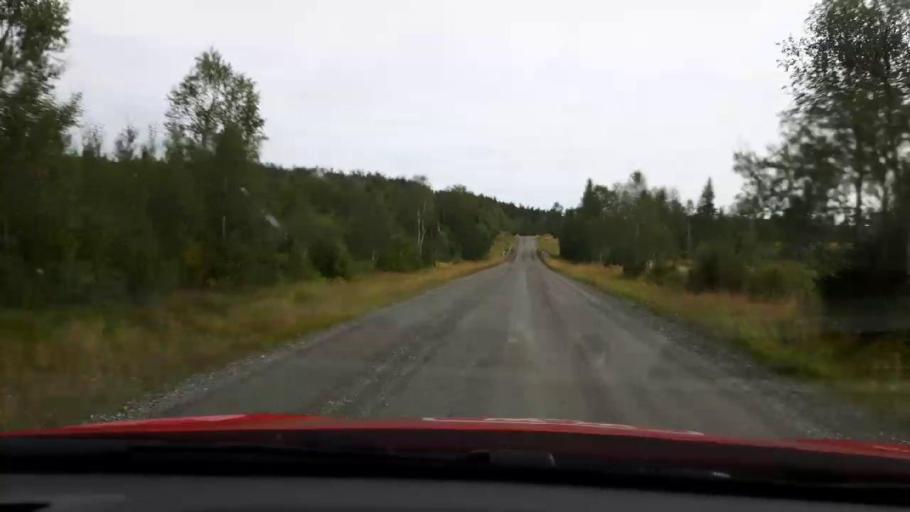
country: SE
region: Jaemtland
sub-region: Are Kommun
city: Are
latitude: 63.7431
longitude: 12.9911
